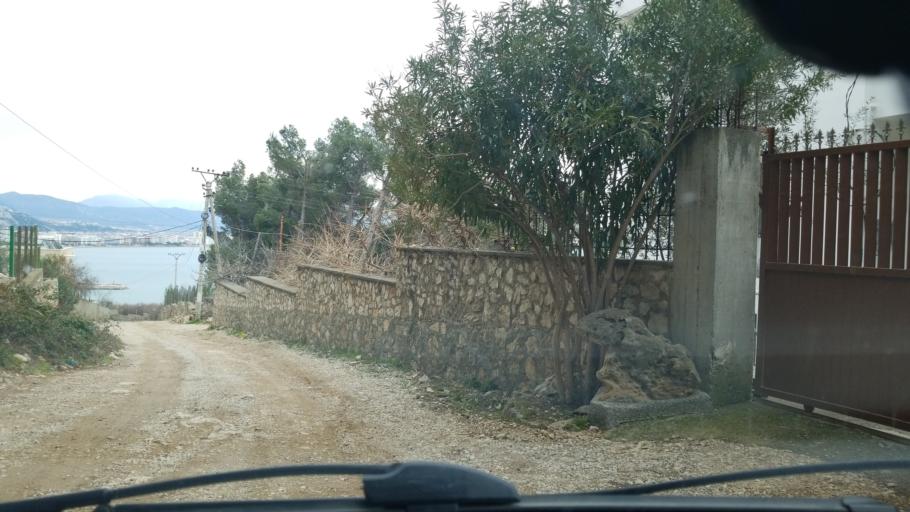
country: AL
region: Lezhe
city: Shengjin
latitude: 41.8126
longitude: 19.5825
